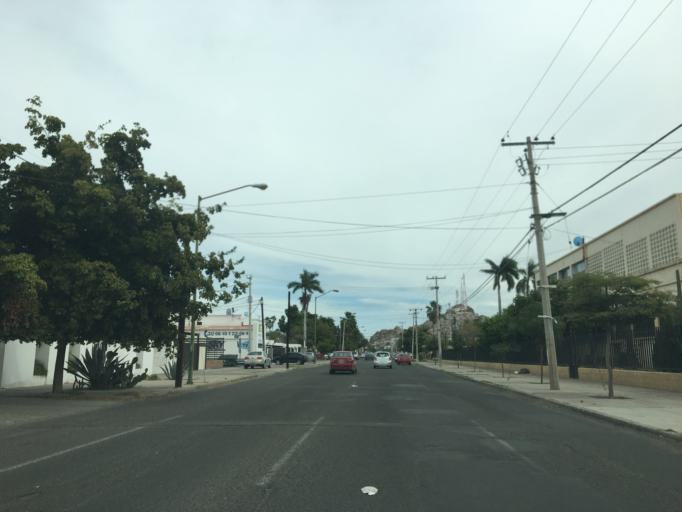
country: MX
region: Sonora
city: Hermosillo
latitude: 29.0737
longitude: -110.9690
